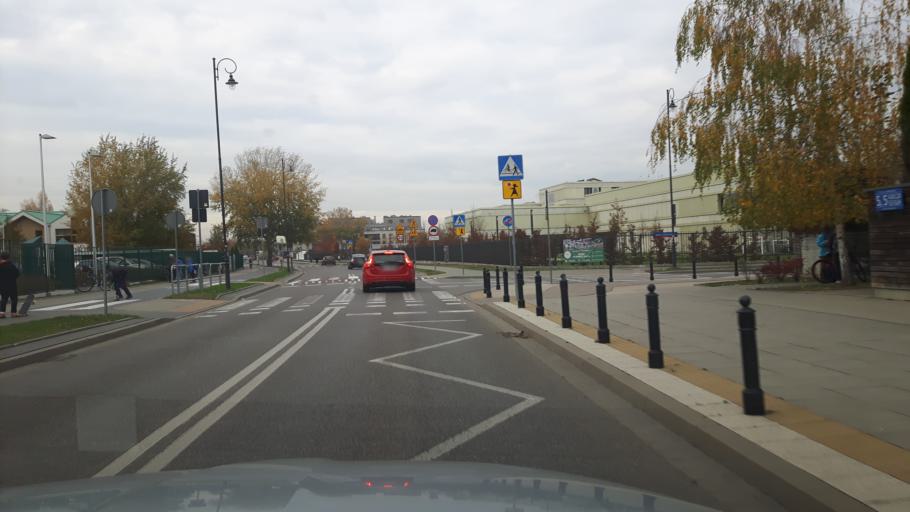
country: PL
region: Masovian Voivodeship
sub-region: Warszawa
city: Wilanow
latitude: 52.1564
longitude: 21.0699
